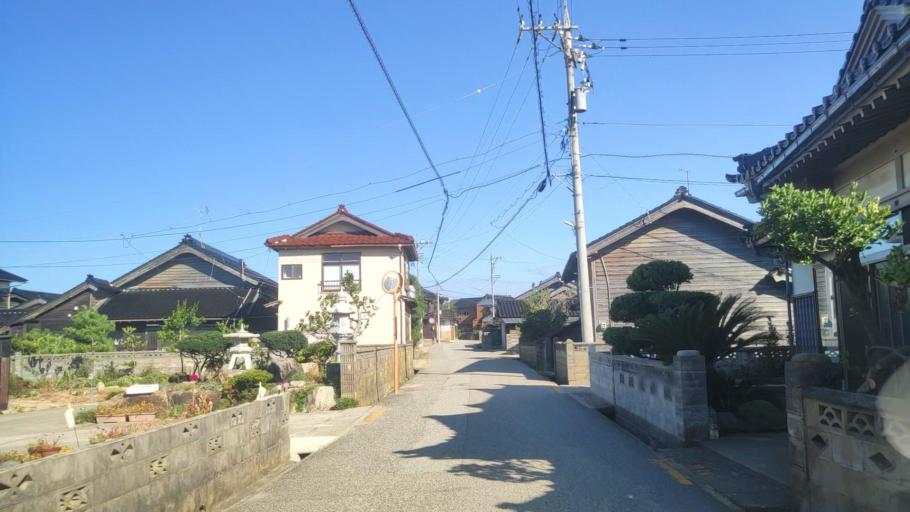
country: JP
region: Ishikawa
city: Hakui
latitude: 36.9468
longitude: 136.7631
